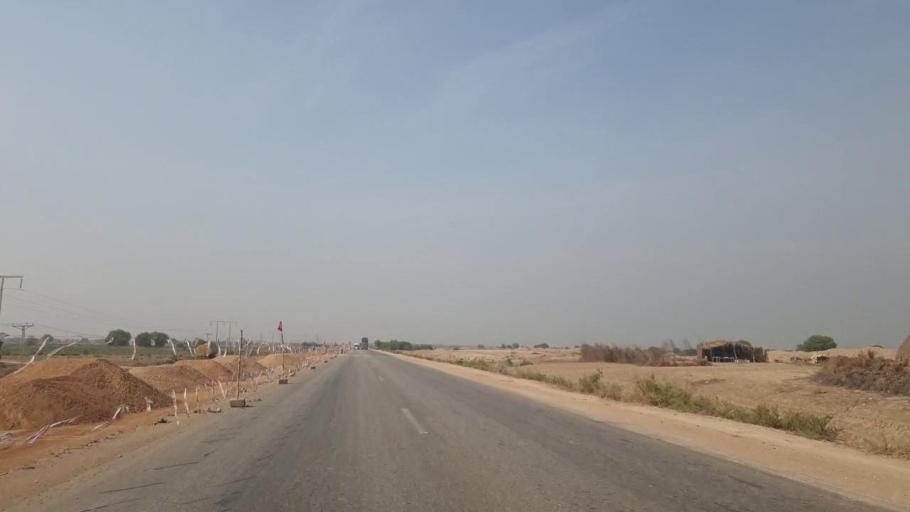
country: PK
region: Sindh
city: Sann
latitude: 26.1439
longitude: 68.0353
